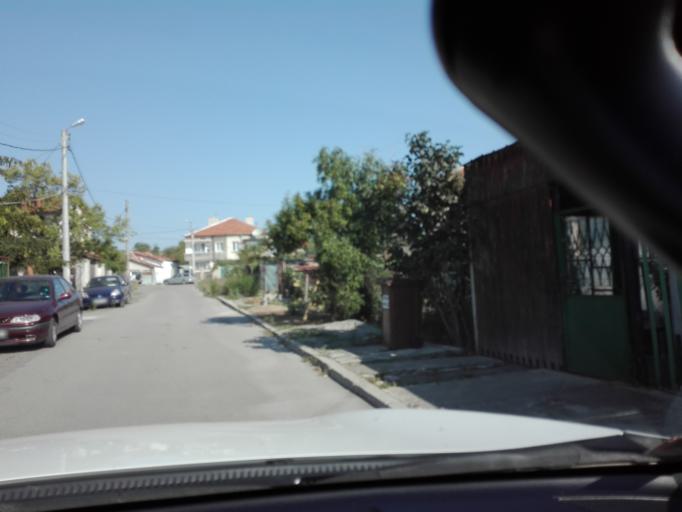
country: BG
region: Burgas
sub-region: Obshtina Kameno
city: Kameno
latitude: 42.6244
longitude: 27.3923
